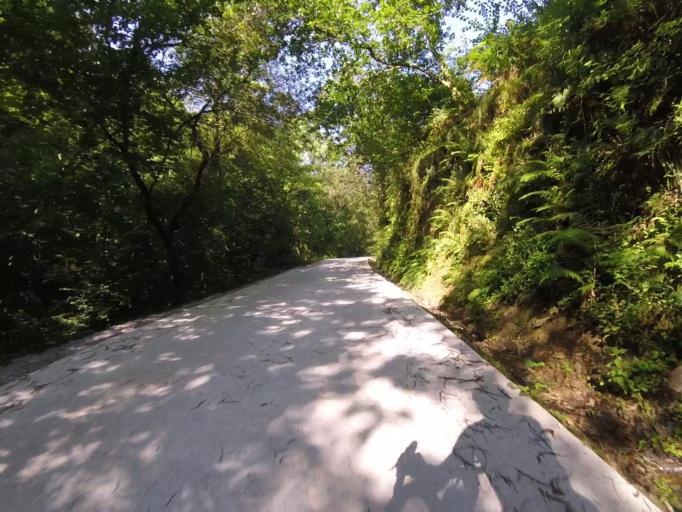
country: ES
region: Basque Country
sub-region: Provincia de Guipuzcoa
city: Astigarraga
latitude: 43.2396
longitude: -1.9297
